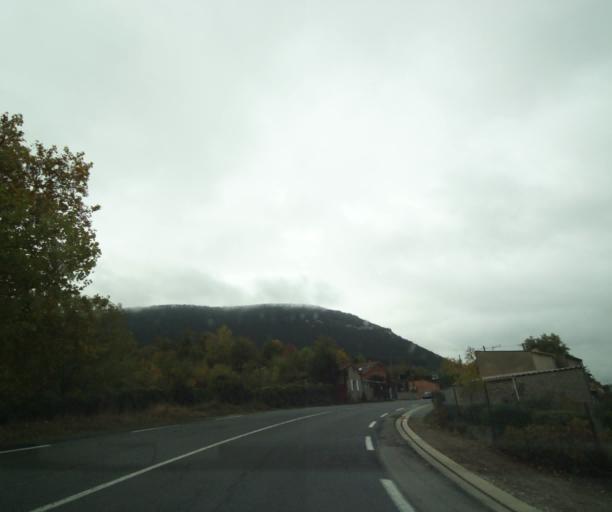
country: FR
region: Midi-Pyrenees
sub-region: Departement de l'Aveyron
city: Millau
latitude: 44.0910
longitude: 3.0906
